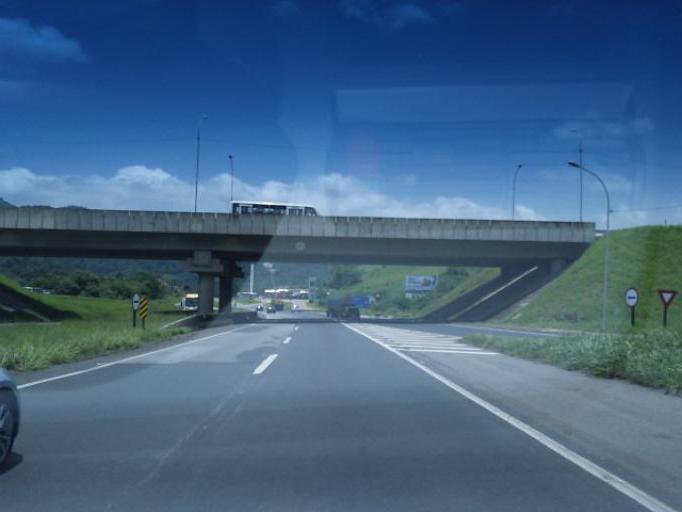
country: BR
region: Sao Paulo
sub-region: Miracatu
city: Miracatu
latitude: -24.2543
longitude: -47.3753
